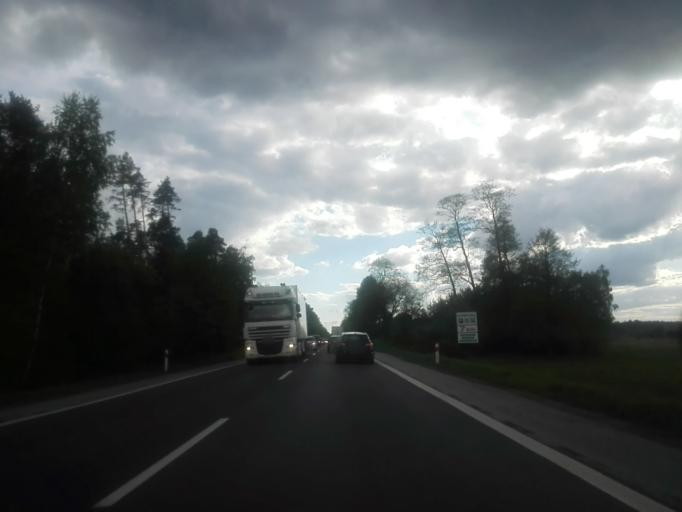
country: PL
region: Masovian Voivodeship
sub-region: Powiat ostrowski
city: Brok
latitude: 52.7520
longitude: 21.7836
